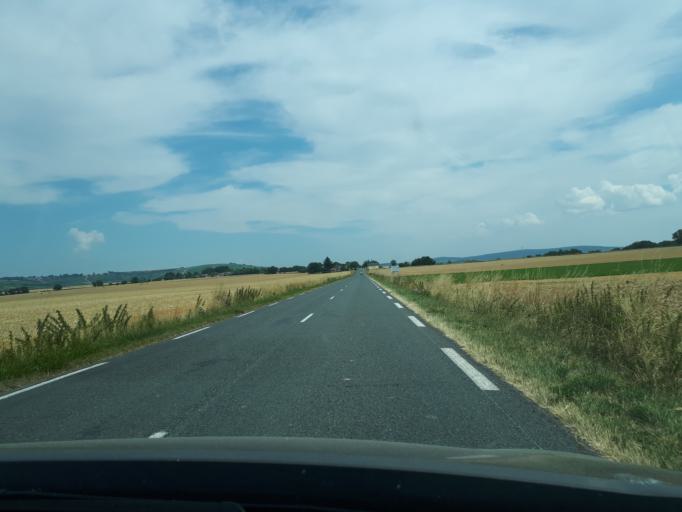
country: FR
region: Centre
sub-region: Departement du Cher
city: Sancerre
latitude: 47.2770
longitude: 2.7458
